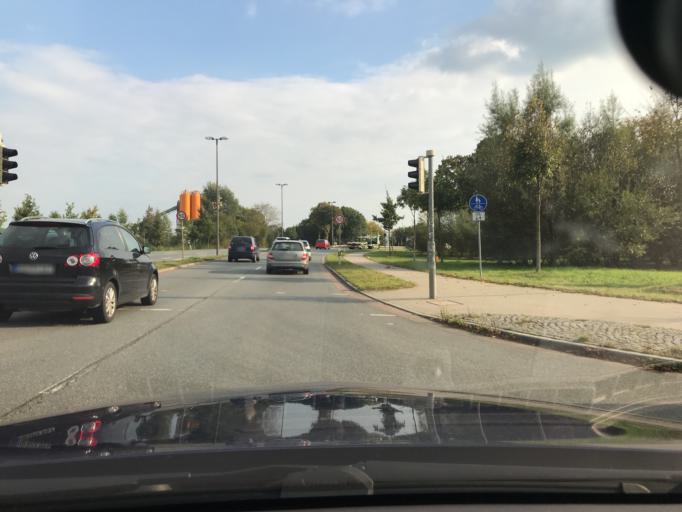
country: DE
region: Bremen
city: Bremen
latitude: 53.0233
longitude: 8.8647
